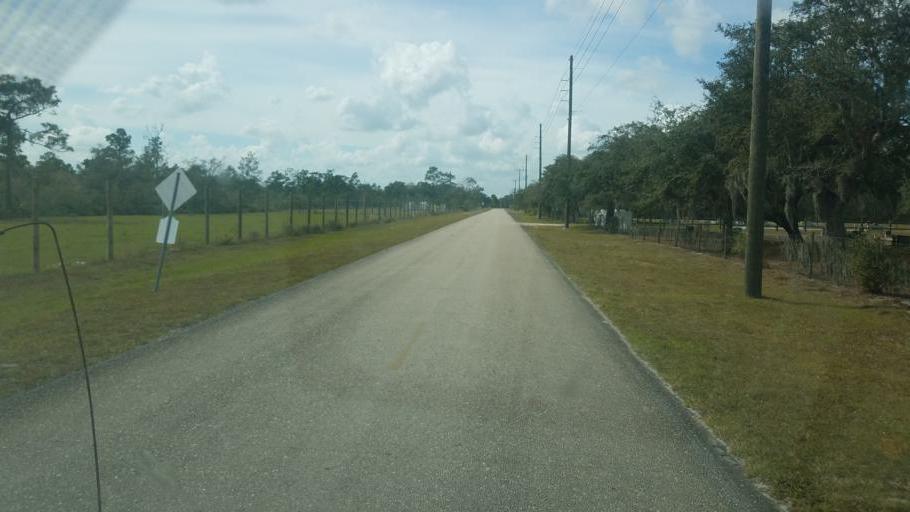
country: US
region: Florida
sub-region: Okeechobee County
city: Cypress Quarters
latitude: 27.5232
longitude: -80.8018
